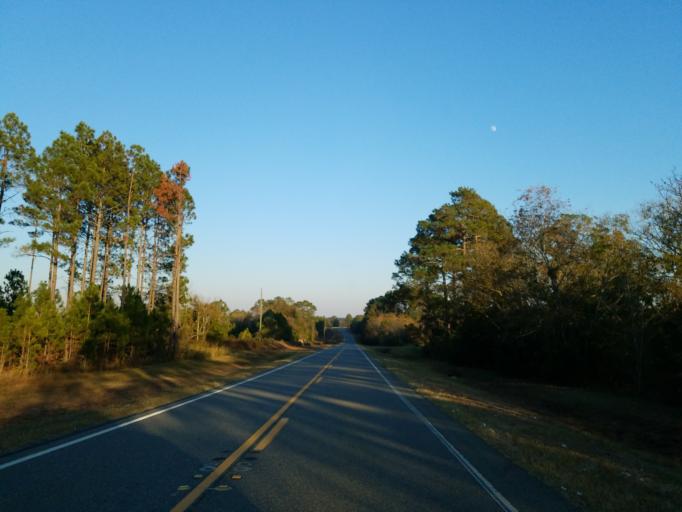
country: US
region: Georgia
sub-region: Wilcox County
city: Rochelle
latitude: 31.8533
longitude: -83.5719
